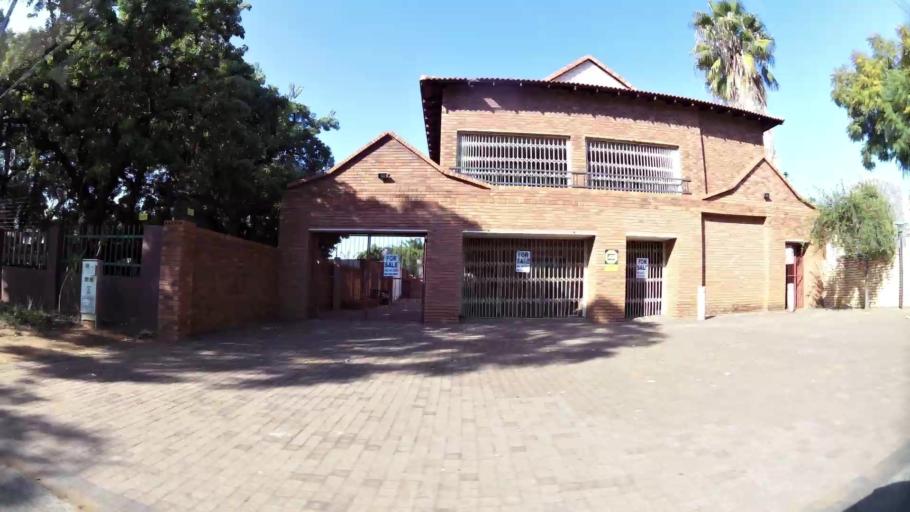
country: ZA
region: Gauteng
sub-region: City of Tshwane Metropolitan Municipality
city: Pretoria
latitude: -25.6700
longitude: 28.1730
